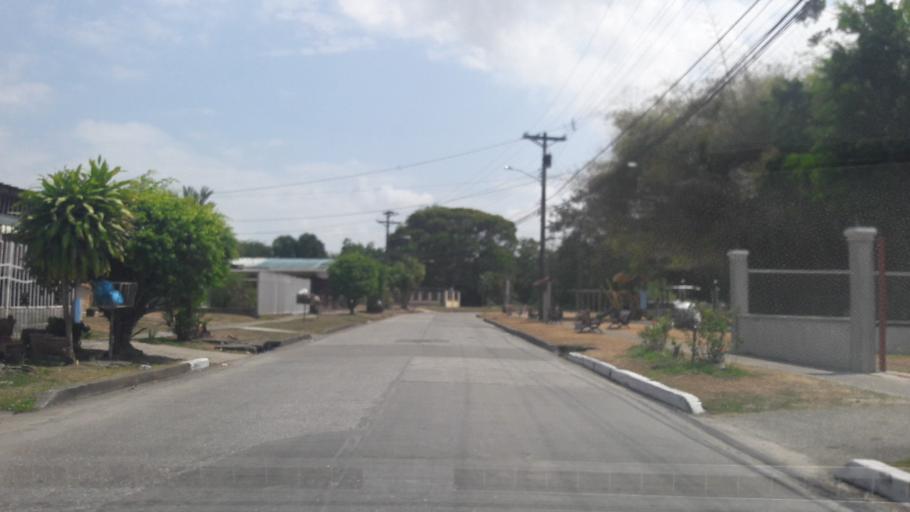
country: PA
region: Panama
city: Alcalde Diaz
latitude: 9.1393
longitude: -79.5529
